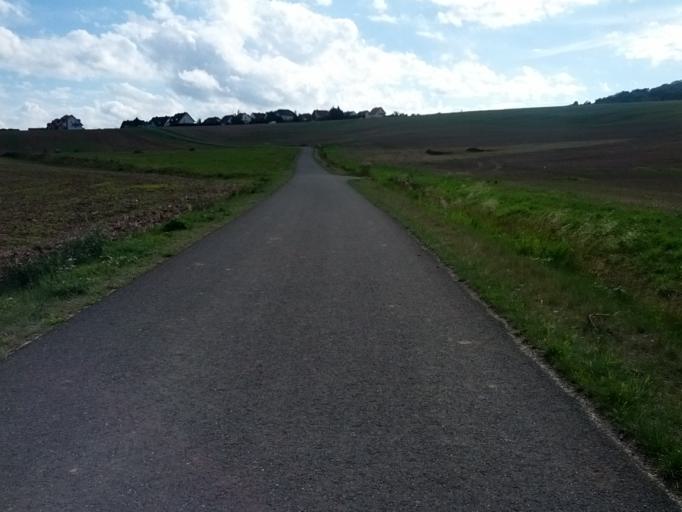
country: DE
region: Thuringia
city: Eisenach
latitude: 51.0130
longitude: 10.3083
